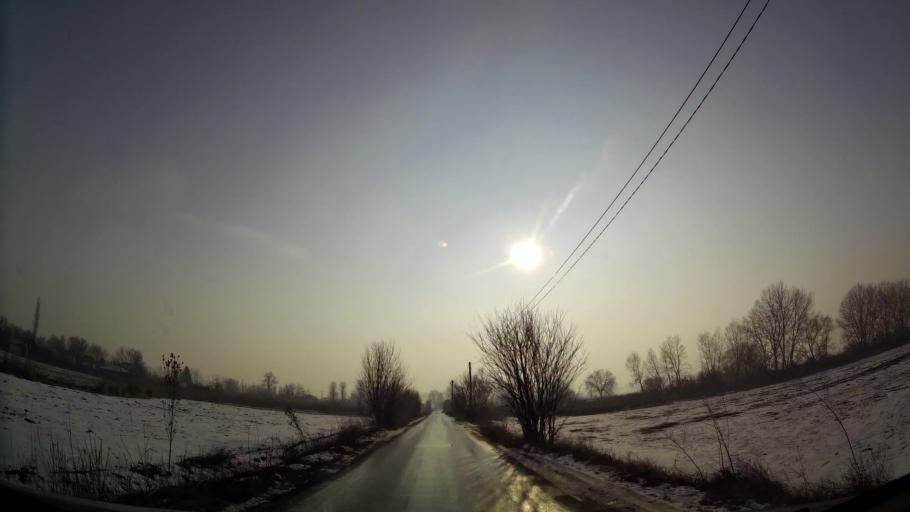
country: MK
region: Petrovec
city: Petrovec
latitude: 41.9483
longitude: 21.5968
